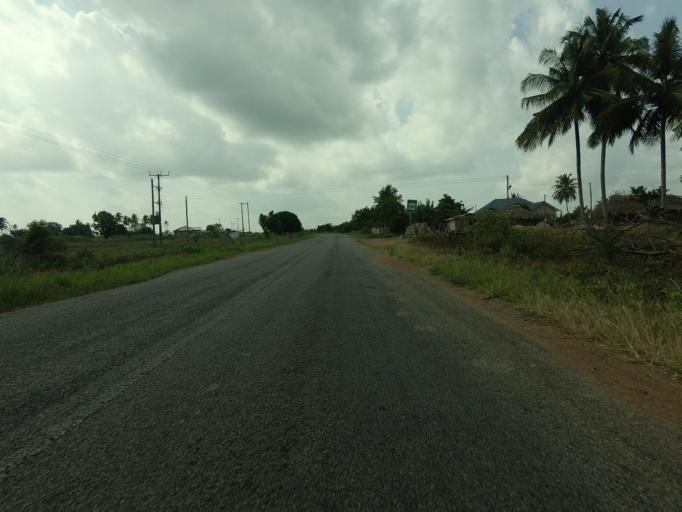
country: GH
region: Volta
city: Ho
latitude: 6.4309
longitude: 0.7322
